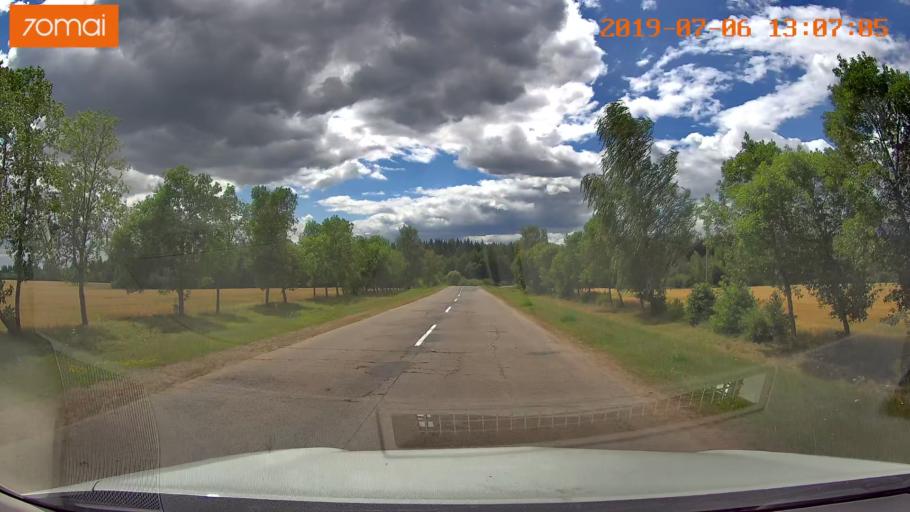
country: BY
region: Minsk
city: Enyerhyetykaw
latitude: 53.6758
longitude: 27.0447
